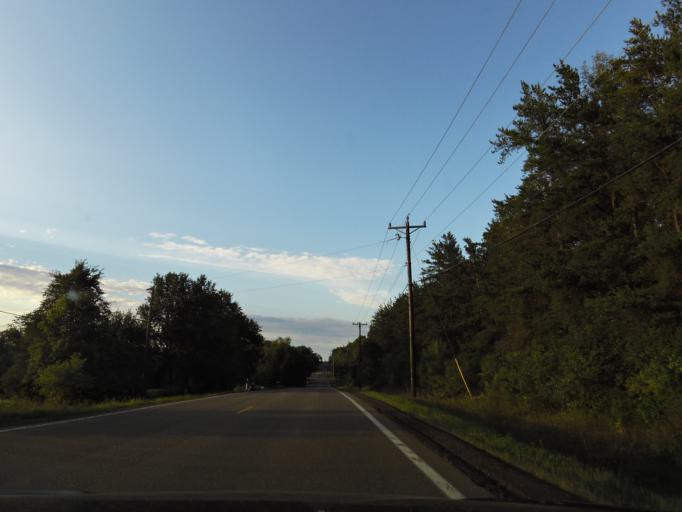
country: US
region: Minnesota
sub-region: Washington County
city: Afton
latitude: 44.9322
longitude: -92.8428
